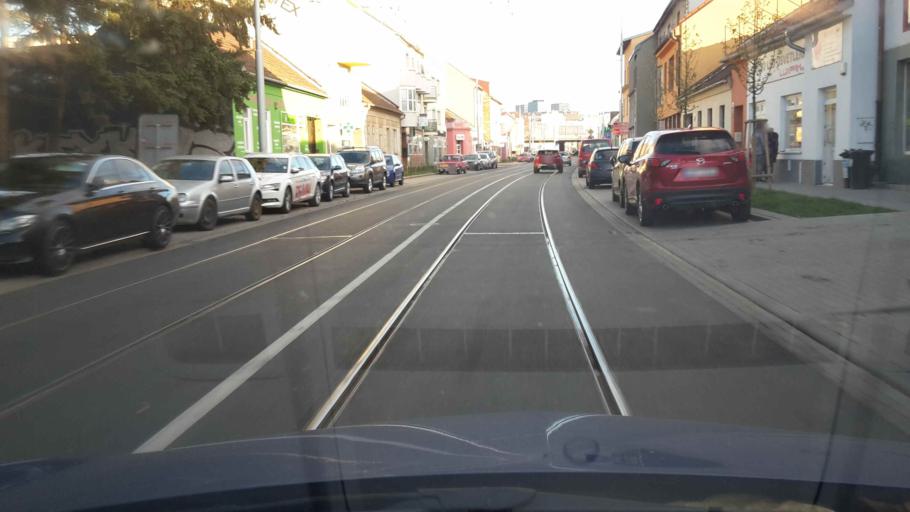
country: CZ
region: South Moravian
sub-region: Mesto Brno
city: Brno
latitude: 49.2144
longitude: 16.5718
